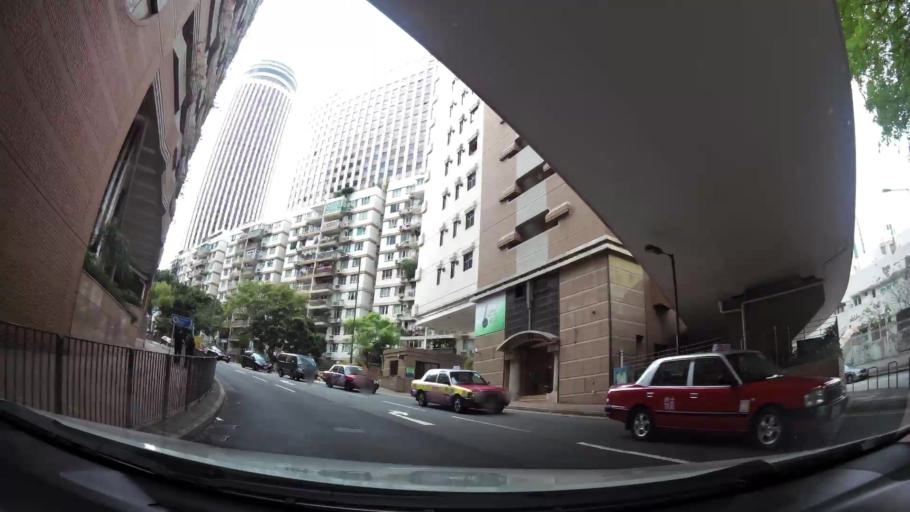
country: HK
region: Wanchai
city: Wan Chai
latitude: 22.2733
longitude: 114.1732
